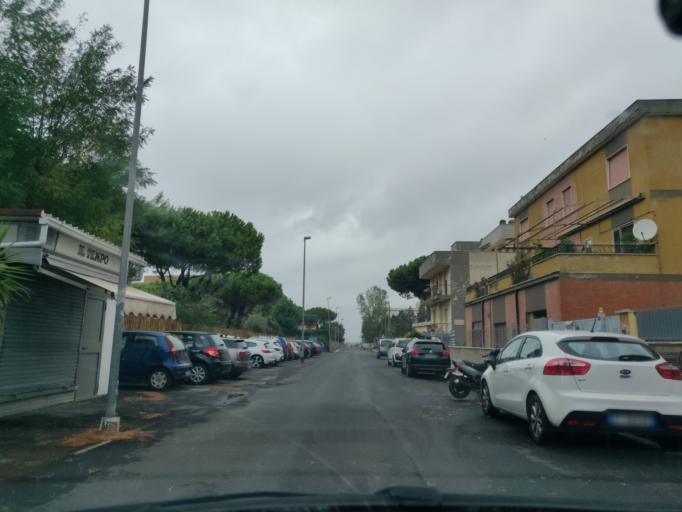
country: IT
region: Latium
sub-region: Citta metropolitana di Roma Capitale
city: Civitavecchia
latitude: 42.1010
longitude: 11.7994
